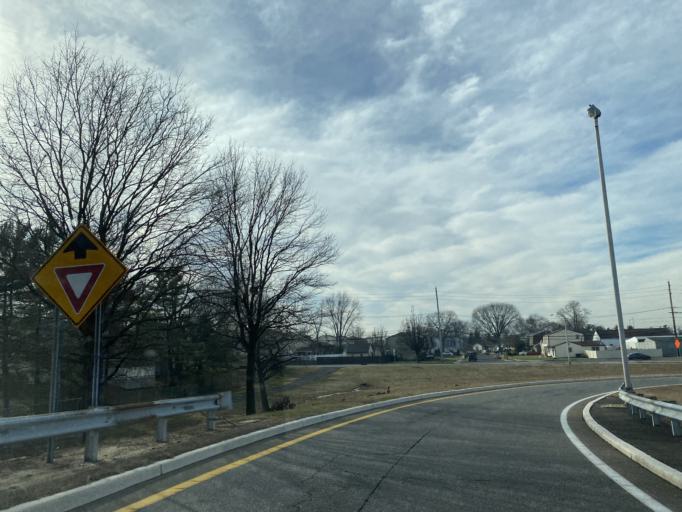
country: US
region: New Jersey
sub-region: Camden County
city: Pennsauken
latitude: 39.9715
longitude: -75.0379
